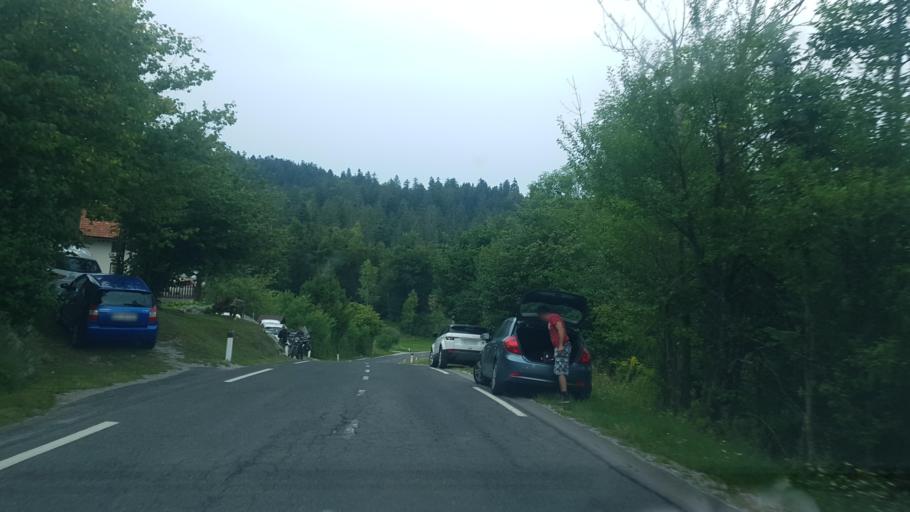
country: SI
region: Logatec
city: Logatec
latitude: 45.8645
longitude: 14.1134
